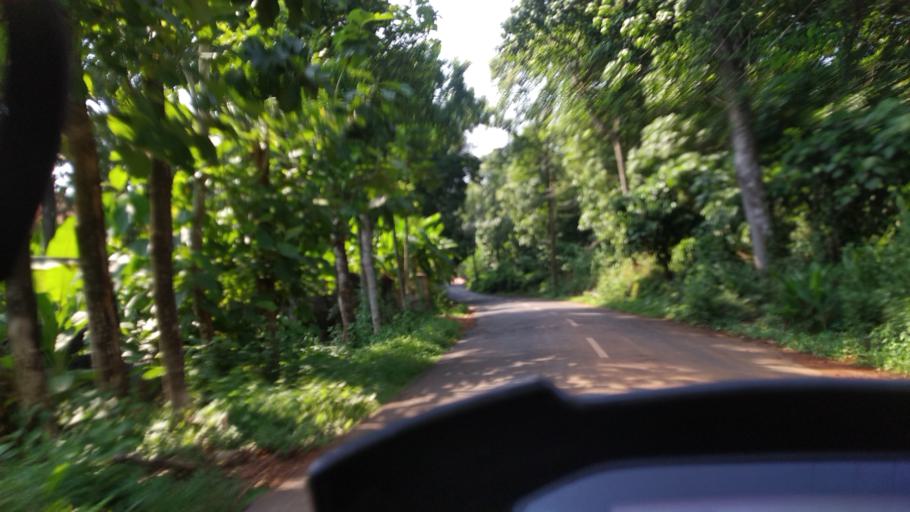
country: IN
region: Kerala
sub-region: Kottayam
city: Palackattumala
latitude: 9.7977
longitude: 76.5884
